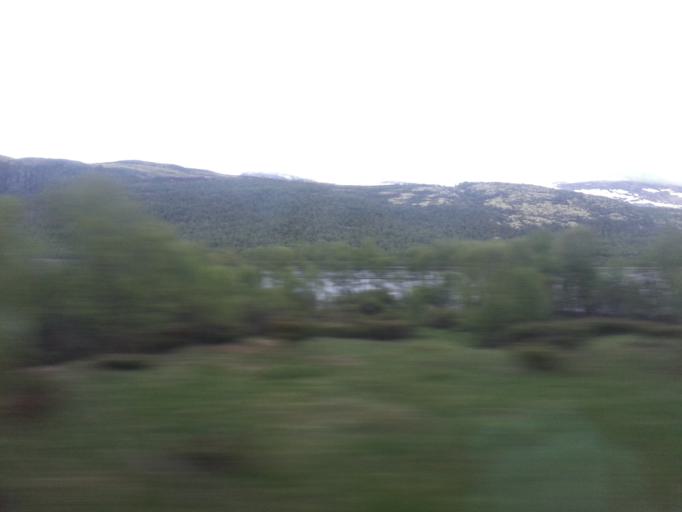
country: NO
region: Oppland
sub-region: Dovre
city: Dovre
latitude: 62.1747
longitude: 9.3820
